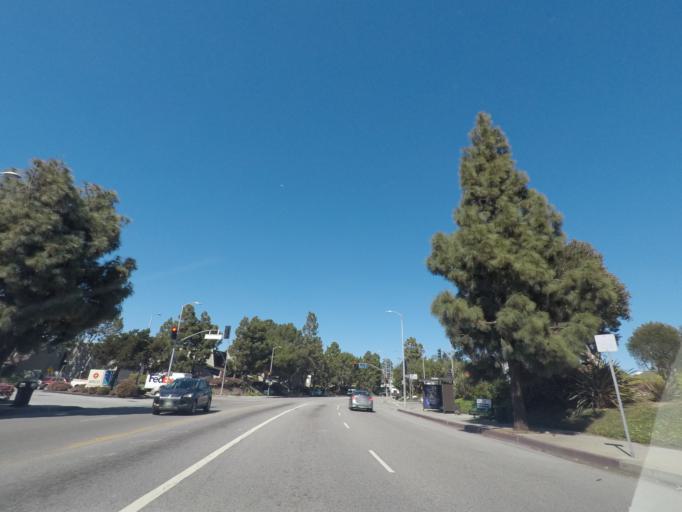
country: US
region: California
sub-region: Los Angeles County
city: Marina del Rey
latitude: 33.9840
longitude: -118.4377
